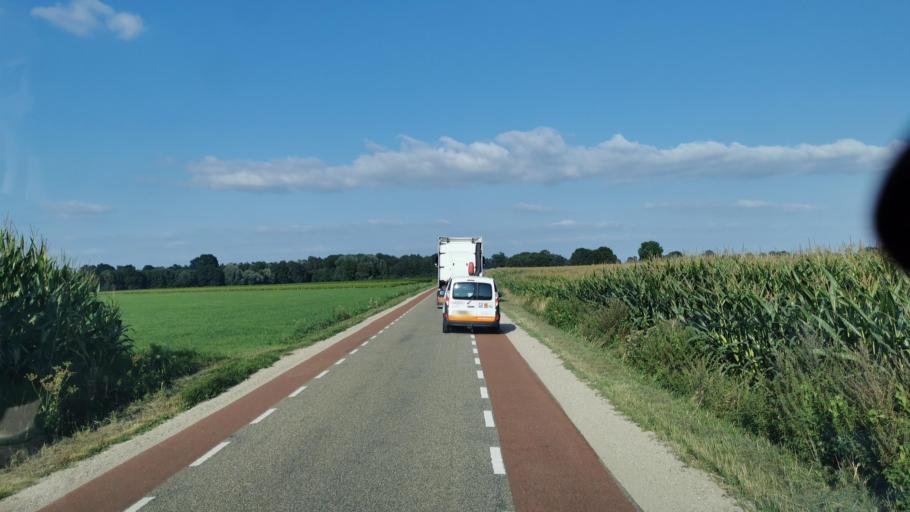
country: NL
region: Overijssel
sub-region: Gemeente Tubbergen
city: Tubbergen
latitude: 52.3430
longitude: 6.8089
